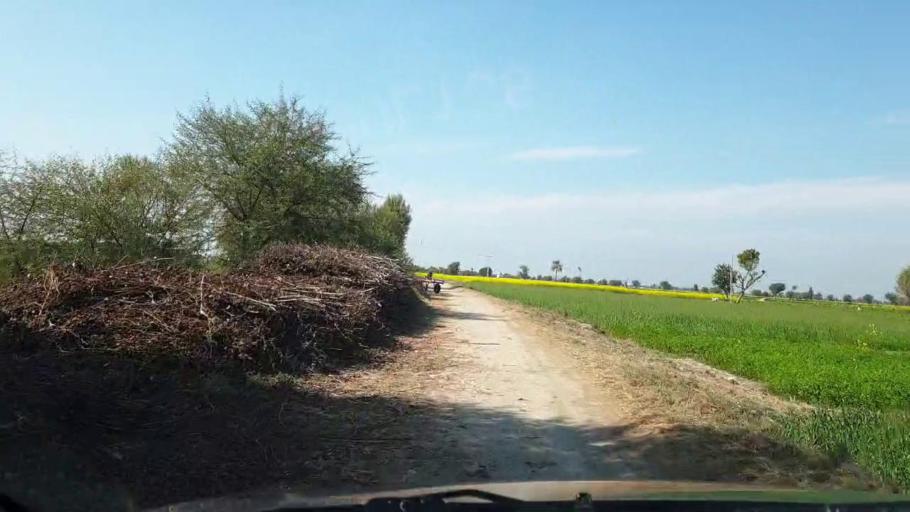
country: PK
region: Sindh
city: Sinjhoro
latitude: 25.9783
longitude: 68.7905
